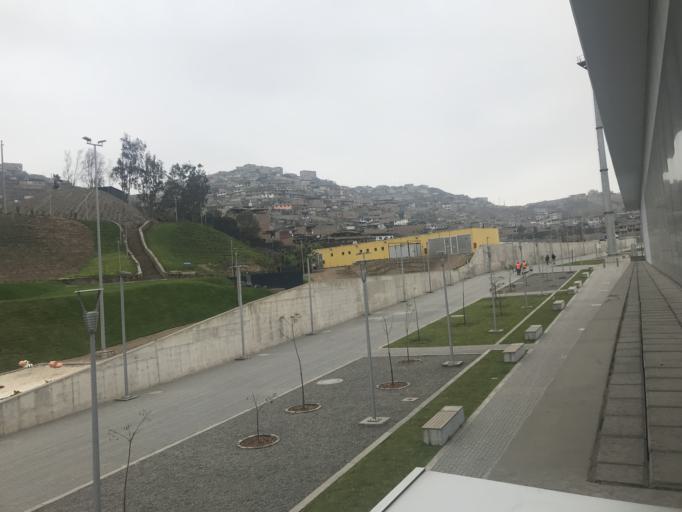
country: PE
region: Lima
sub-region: Lima
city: Surco
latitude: -12.1484
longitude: -76.9533
